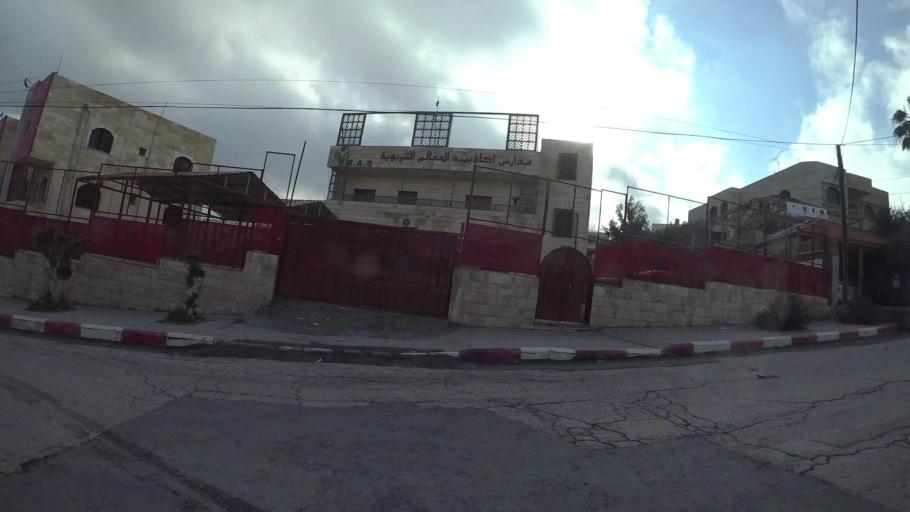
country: JO
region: Amman
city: Al Jubayhah
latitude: 32.0542
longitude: 35.8990
